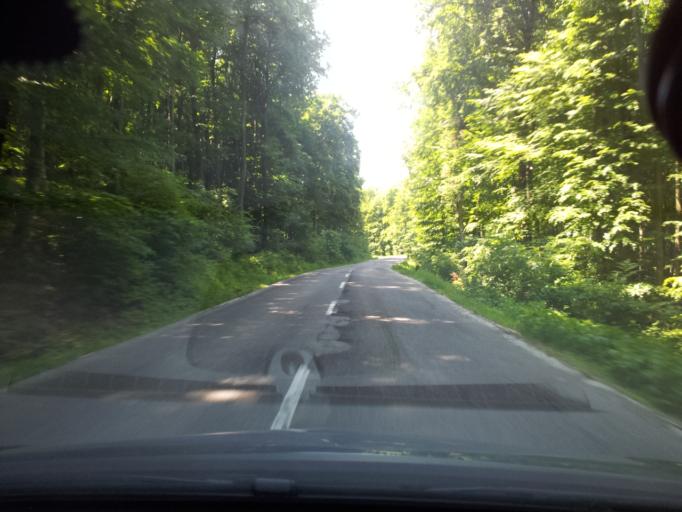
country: SK
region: Nitriansky
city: Partizanske
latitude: 48.5363
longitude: 18.4439
